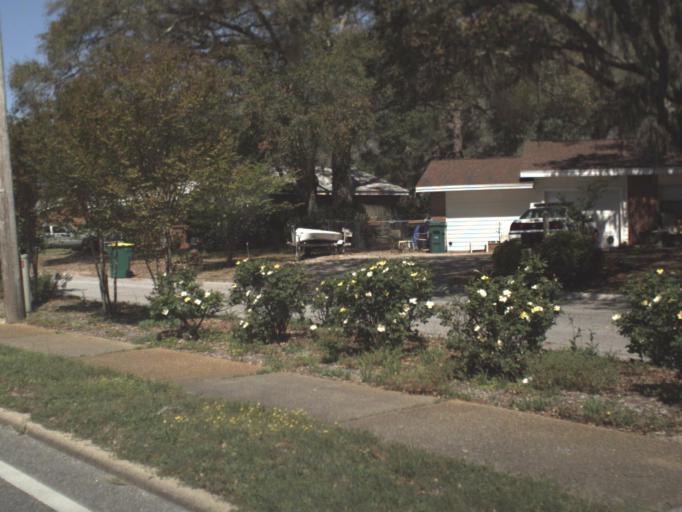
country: US
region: Florida
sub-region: Okaloosa County
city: Mary Esther
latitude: 30.4092
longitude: -86.6505
